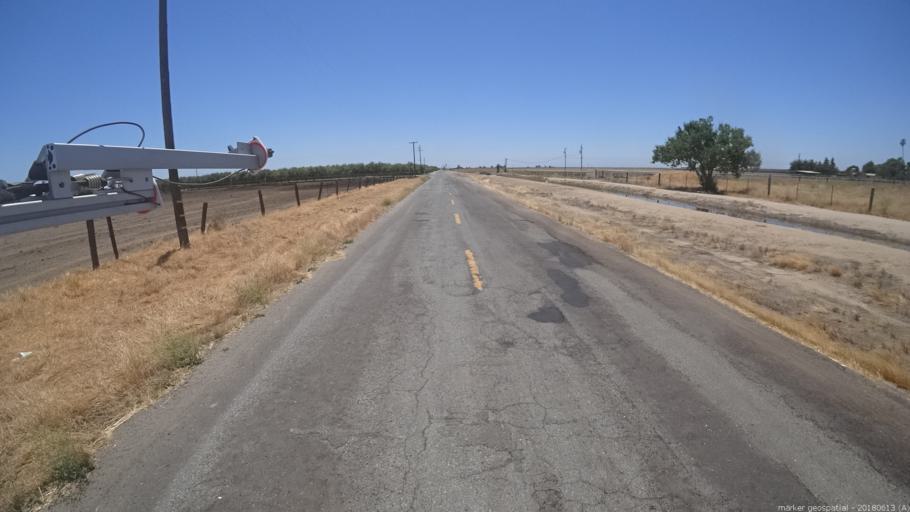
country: US
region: California
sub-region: Madera County
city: Chowchilla
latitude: 37.0195
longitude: -120.2924
